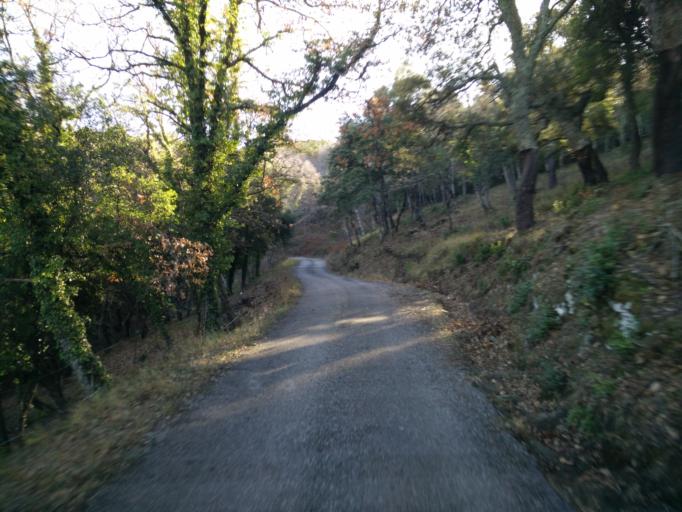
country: FR
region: Provence-Alpes-Cote d'Azur
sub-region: Departement du Var
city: Gonfaron
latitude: 43.2950
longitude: 6.2886
